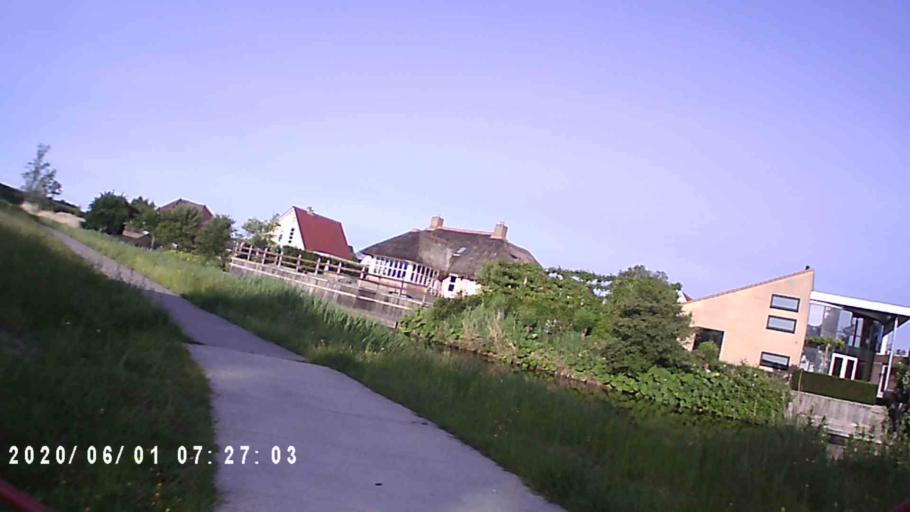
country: NL
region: Friesland
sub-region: Gemeente Dongeradeel
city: Dokkum
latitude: 53.3184
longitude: 6.0178
